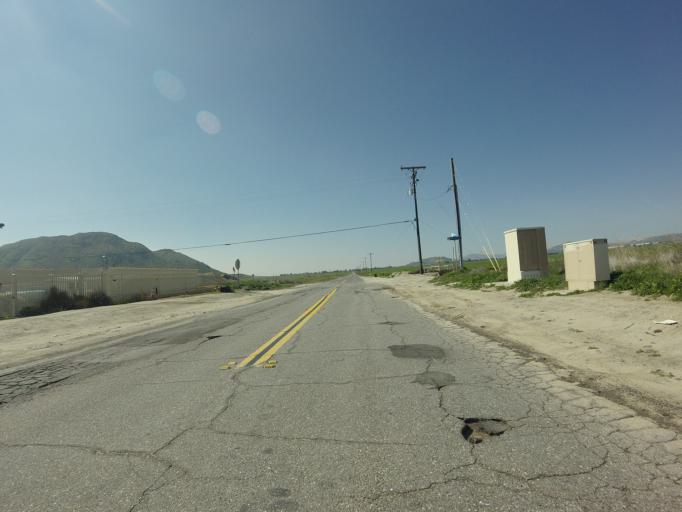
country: US
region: California
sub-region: Riverside County
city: Lakeview
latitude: 33.9195
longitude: -117.1208
